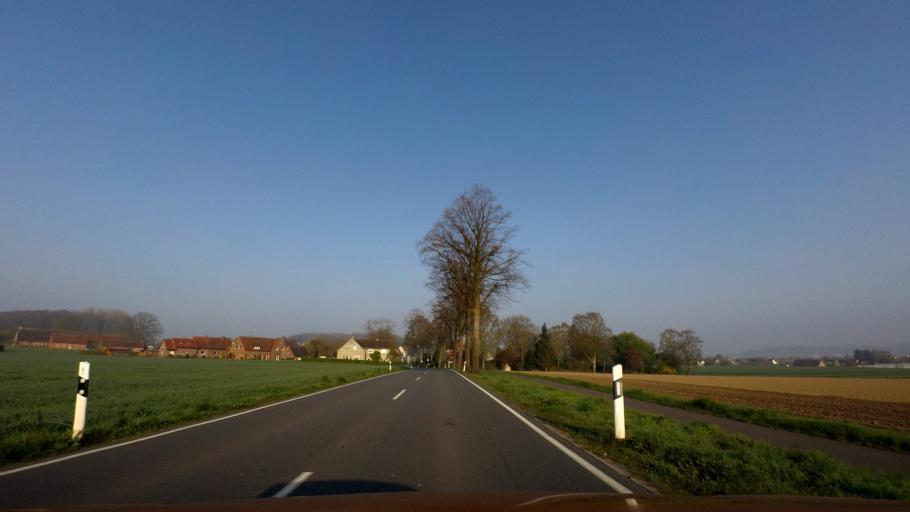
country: DE
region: Lower Saxony
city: Melle
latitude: 52.1877
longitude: 8.3632
